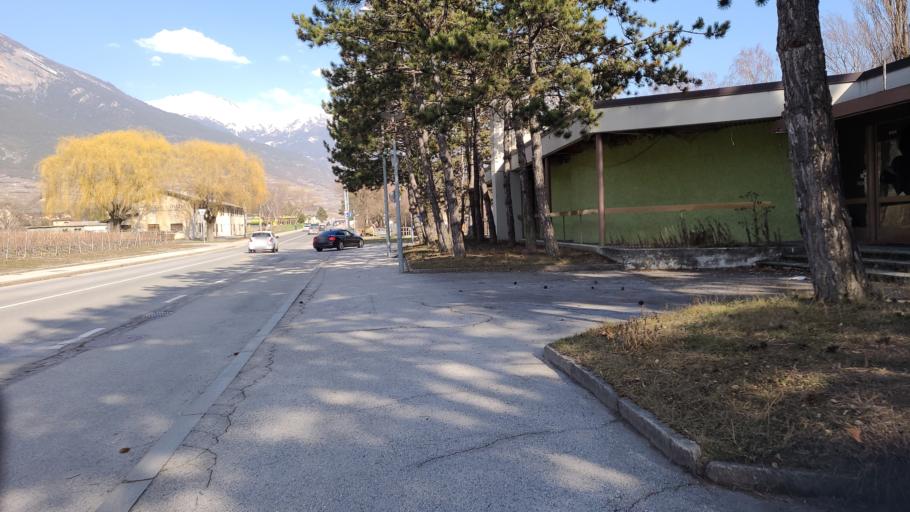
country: CH
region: Valais
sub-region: Sierre District
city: Veyras
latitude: 46.2978
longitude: 7.5538
